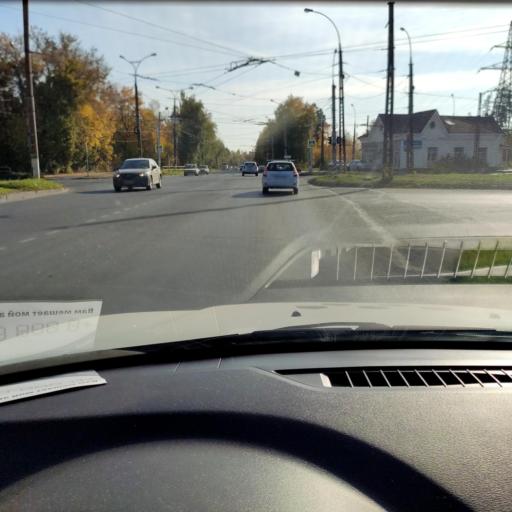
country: RU
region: Samara
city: Tol'yatti
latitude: 53.5058
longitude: 49.3908
